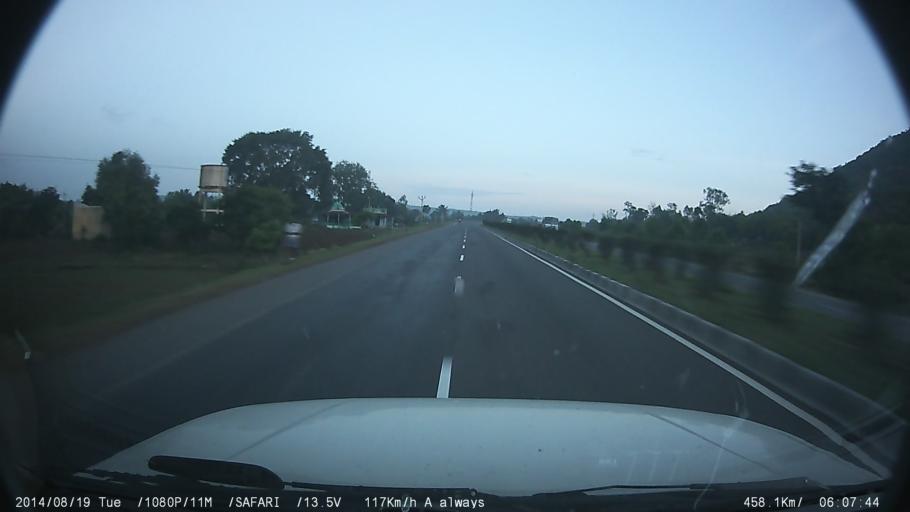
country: IN
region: Tamil Nadu
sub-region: Salem
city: Omalur
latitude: 11.9050
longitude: 78.0609
